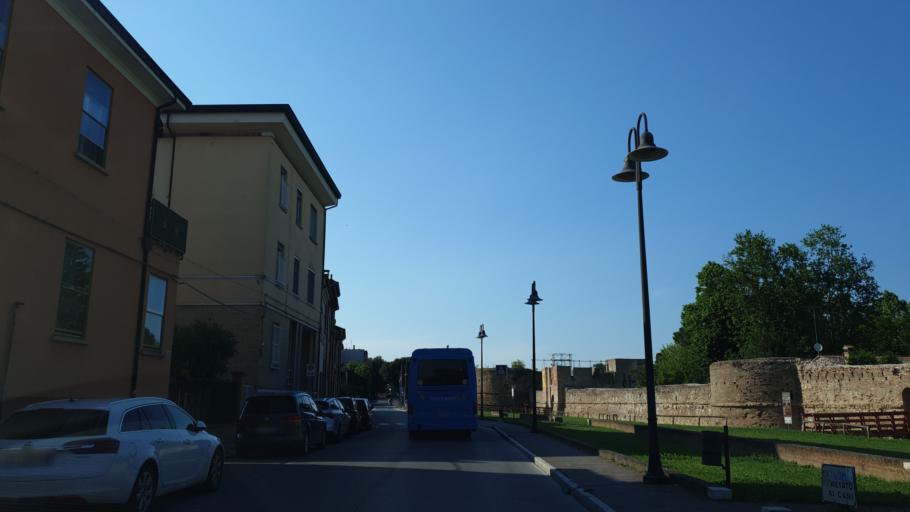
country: IT
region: Emilia-Romagna
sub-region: Provincia di Ravenna
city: Ravenna
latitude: 44.4212
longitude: 12.2053
